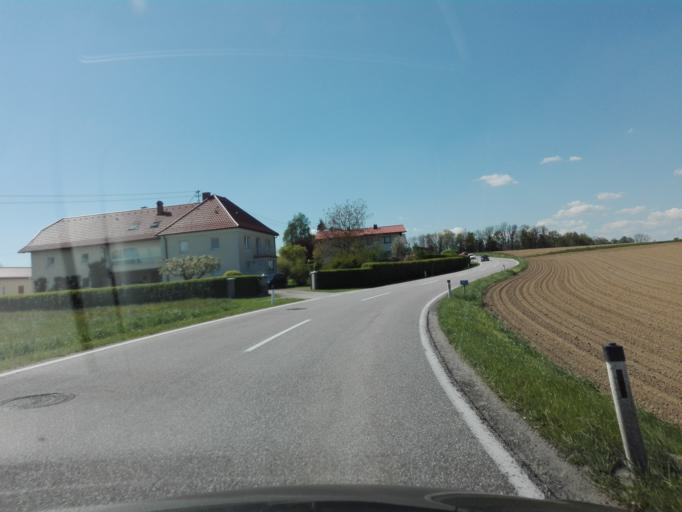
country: AT
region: Upper Austria
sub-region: Politischer Bezirk Grieskirchen
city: Bad Schallerbach
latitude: 48.3195
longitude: 13.8926
